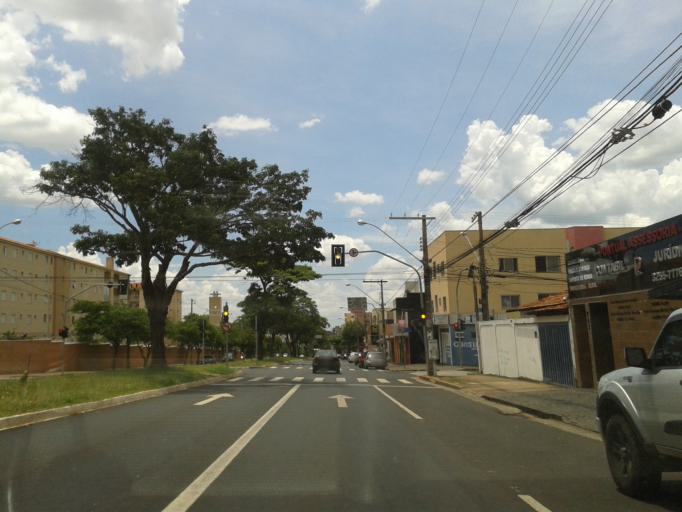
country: BR
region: Minas Gerais
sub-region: Uberlandia
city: Uberlandia
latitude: -18.9175
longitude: -48.2522
